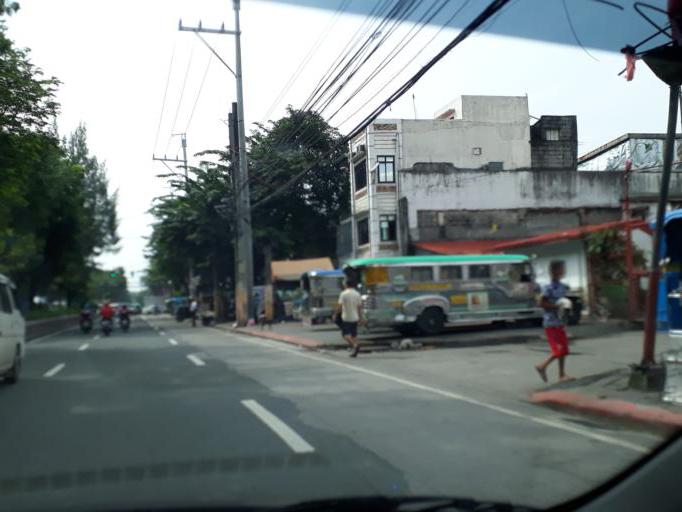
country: PH
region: Metro Manila
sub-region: City of Manila
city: Manila
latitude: 14.6143
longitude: 120.9883
